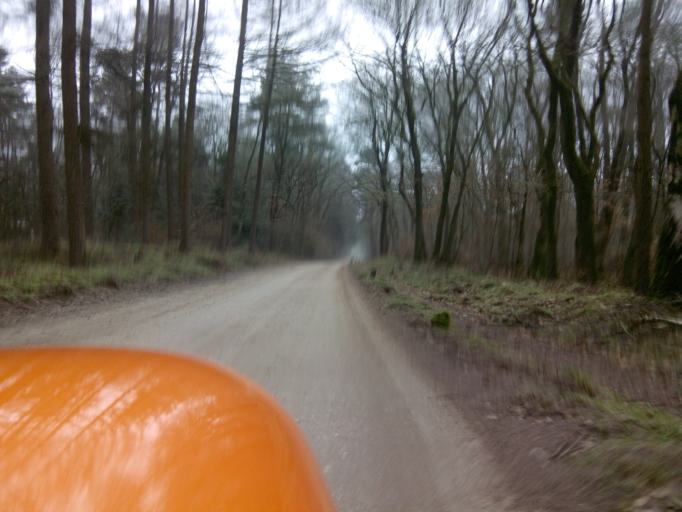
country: NL
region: Gelderland
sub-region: Gemeente Barneveld
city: Garderen
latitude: 52.2231
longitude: 5.6930
